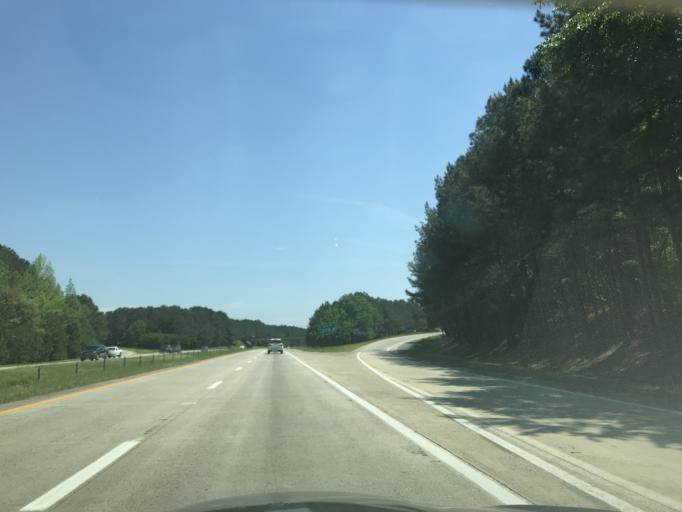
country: US
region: North Carolina
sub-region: Johnston County
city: Benson
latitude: 35.5194
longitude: -78.5598
